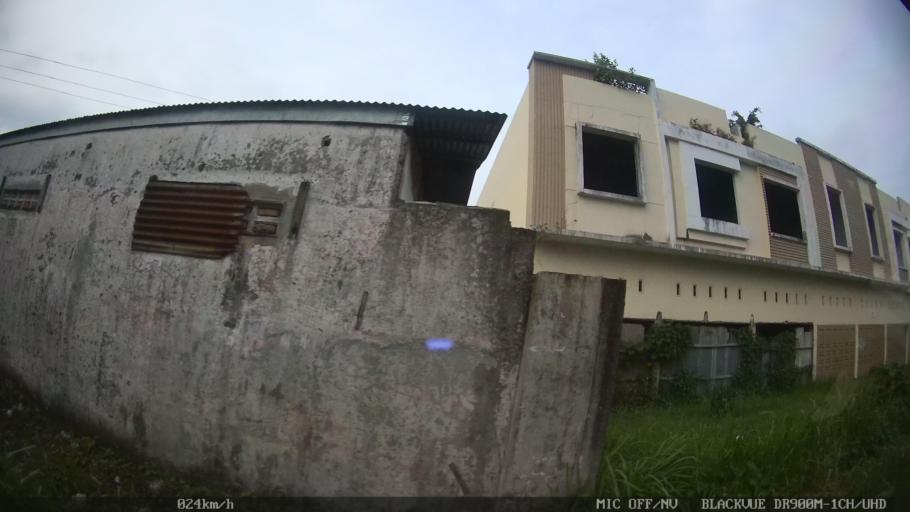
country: ID
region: North Sumatra
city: Sunggal
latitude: 3.5810
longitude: 98.6037
